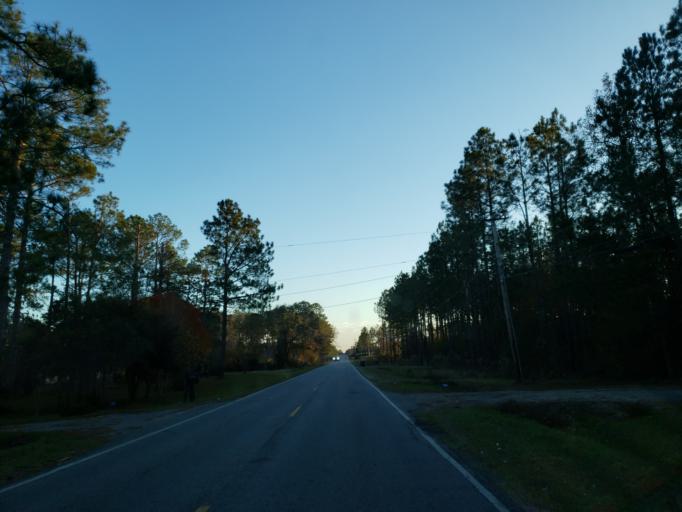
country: US
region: Georgia
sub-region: Crisp County
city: Cordele
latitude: 31.9469
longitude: -83.7658
